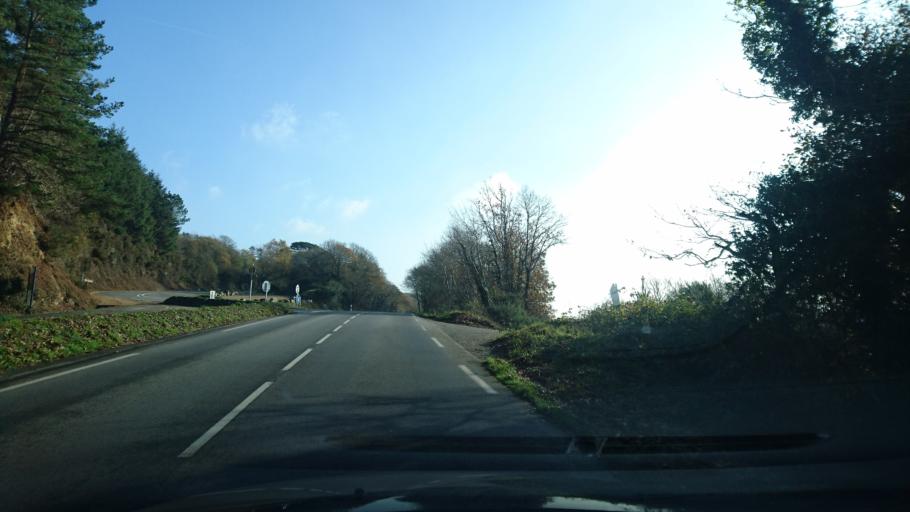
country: FR
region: Brittany
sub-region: Departement du Finistere
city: Logonna-Daoulas
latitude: 48.2744
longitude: -4.2672
